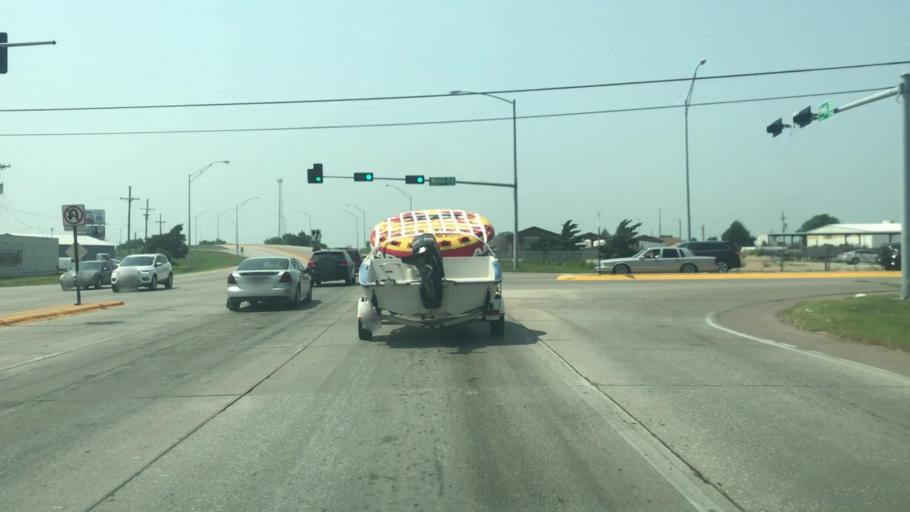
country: US
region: Nebraska
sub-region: Hall County
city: Grand Island
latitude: 40.9155
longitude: -98.3781
